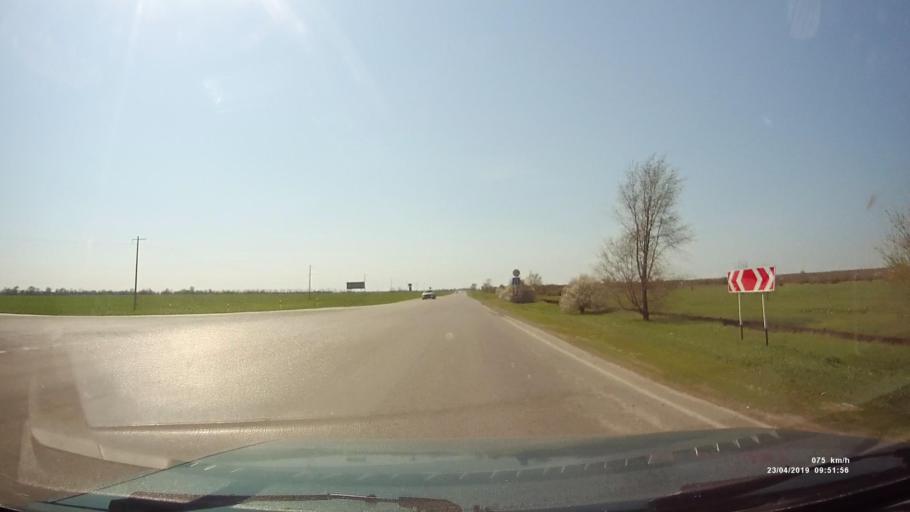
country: RU
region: Rostov
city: Orlovskiy
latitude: 46.8502
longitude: 42.0433
